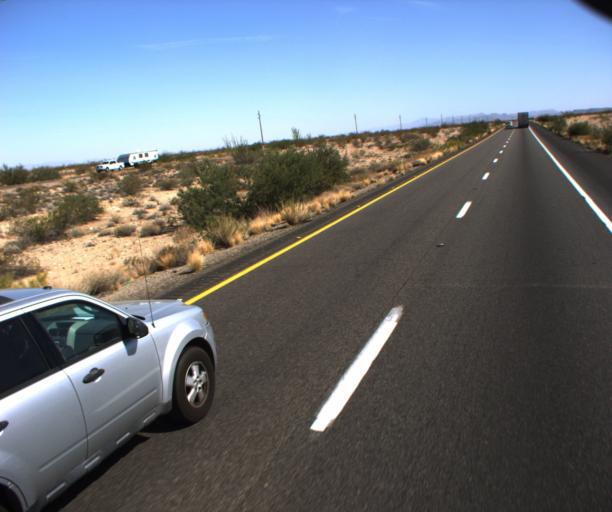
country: US
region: Arizona
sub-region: Mohave County
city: Kingman
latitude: 34.9834
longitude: -114.1395
